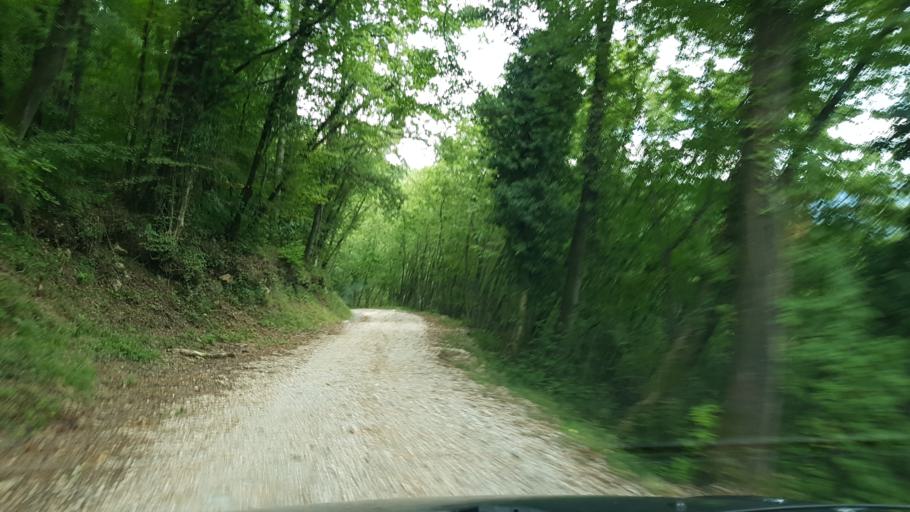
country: SI
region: Kanal
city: Deskle
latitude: 46.0558
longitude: 13.5811
